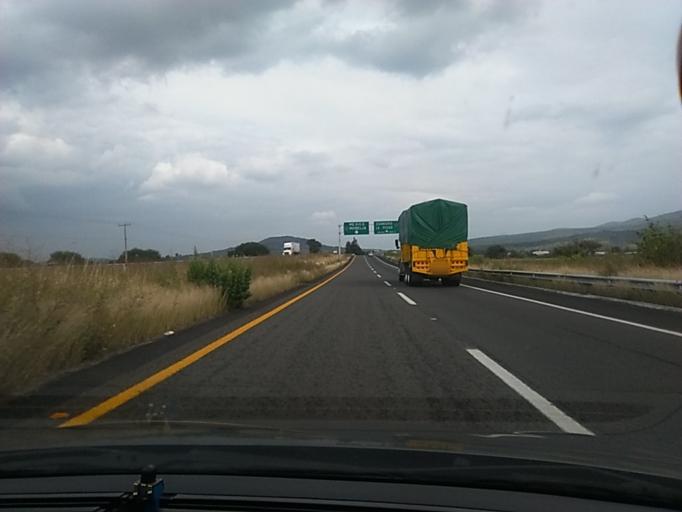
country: MX
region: Michoacan
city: Ecuandureo
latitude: 20.1752
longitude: -102.2073
